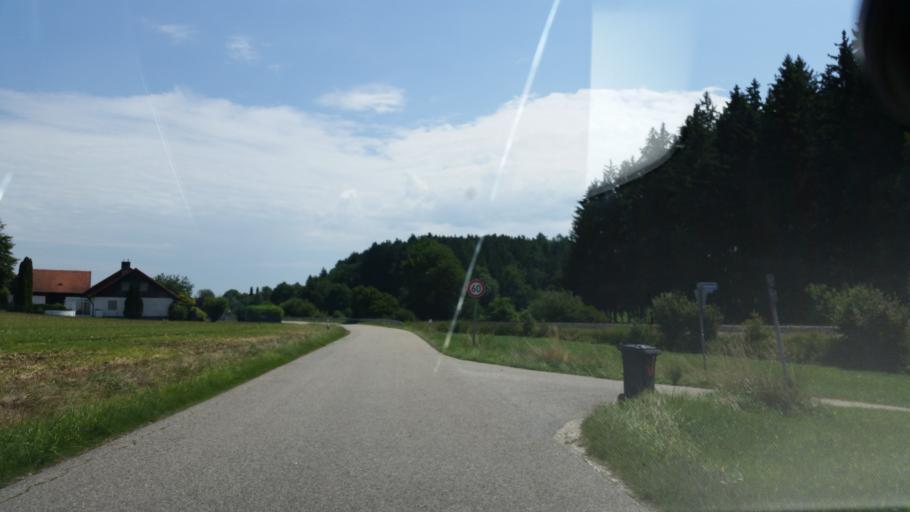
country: DE
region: Bavaria
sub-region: Lower Bavaria
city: Geisenhausen
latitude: 48.4584
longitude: 12.2949
